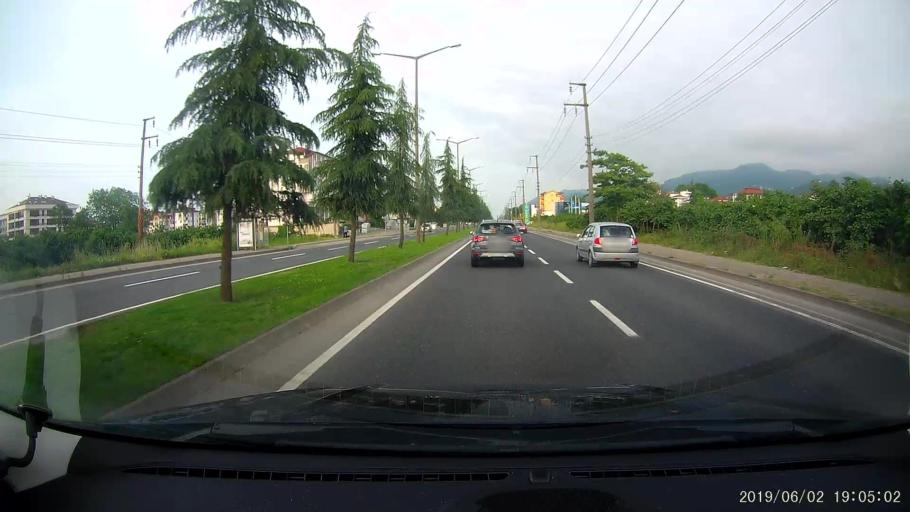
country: TR
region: Ordu
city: Ordu
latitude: 40.9774
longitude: 37.9479
